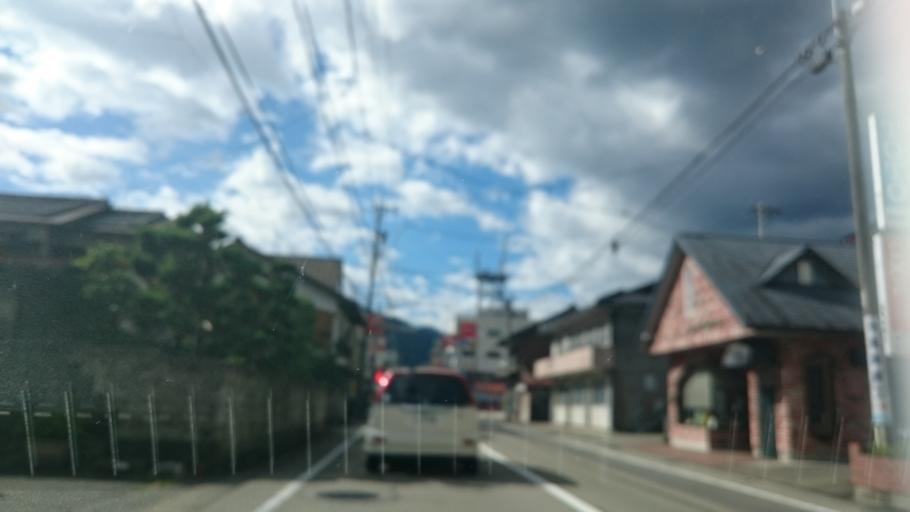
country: JP
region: Gifu
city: Gujo
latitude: 35.8029
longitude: 137.2464
